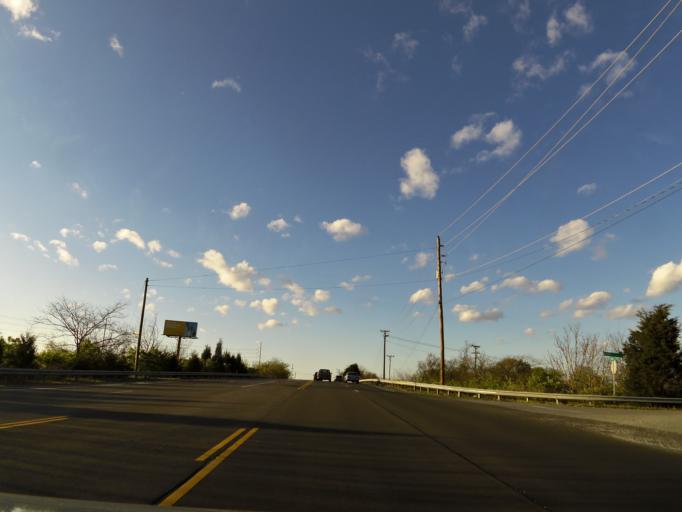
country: US
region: Tennessee
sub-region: Davidson County
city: Goodlettsville
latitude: 36.2875
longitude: -86.6931
